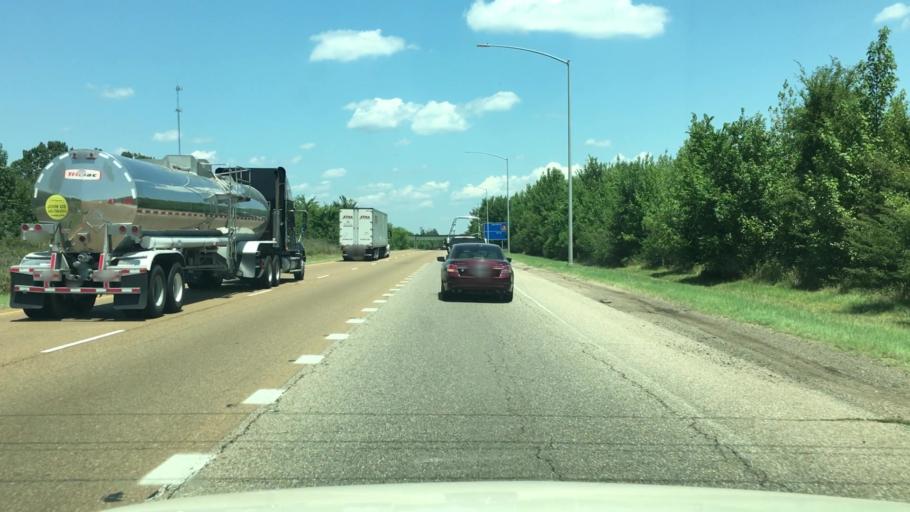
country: US
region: Arkansas
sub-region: Nevada County
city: Prescott
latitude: 33.8135
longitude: -93.4189
